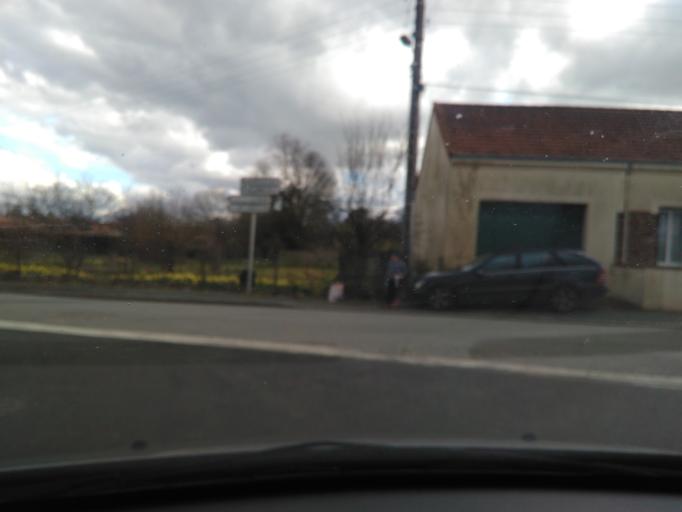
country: FR
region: Pays de la Loire
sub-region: Departement de la Vendee
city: Saint-Martin-des-Noyers
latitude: 46.7224
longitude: -1.1771
